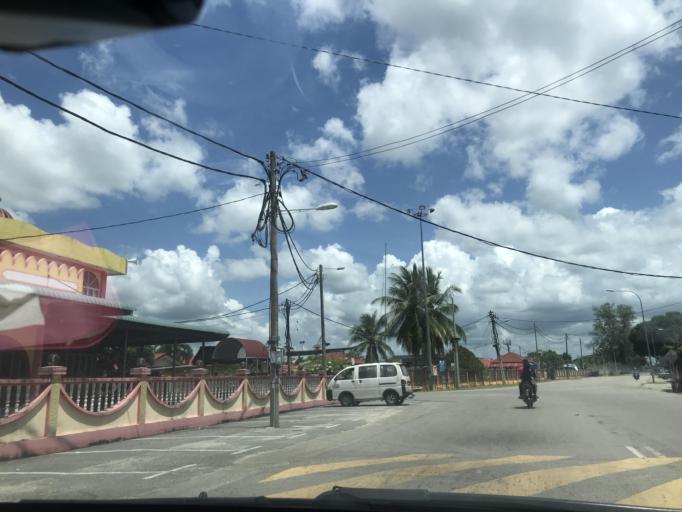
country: TH
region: Narathiwat
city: Tak Bai
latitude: 6.2304
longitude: 102.0953
